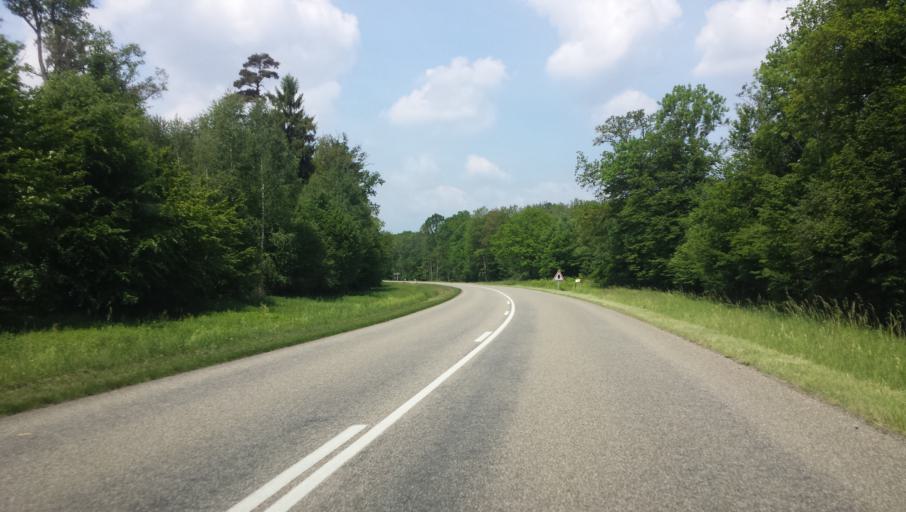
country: DE
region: Rheinland-Pfalz
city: Scheibenhardt
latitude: 48.9861
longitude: 8.1067
